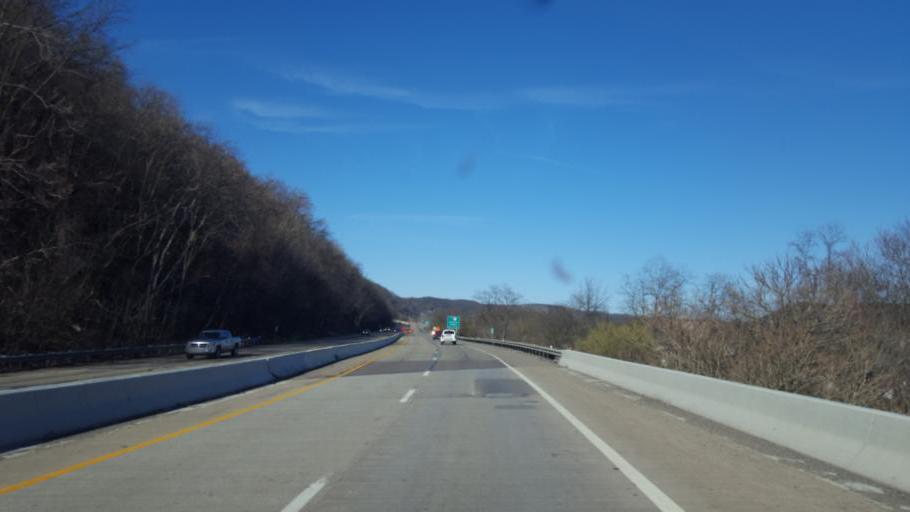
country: US
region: Ohio
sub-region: Columbiana County
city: Wellsville
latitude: 40.6051
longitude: -80.6531
